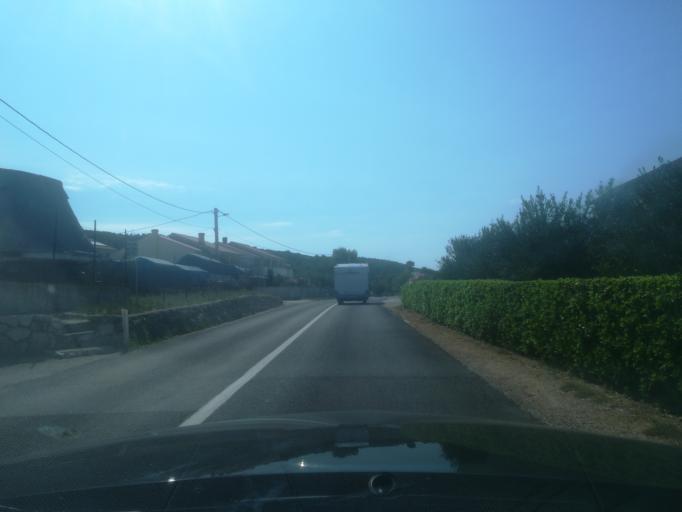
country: HR
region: Primorsko-Goranska
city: Banjol
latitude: 44.7265
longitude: 14.8170
